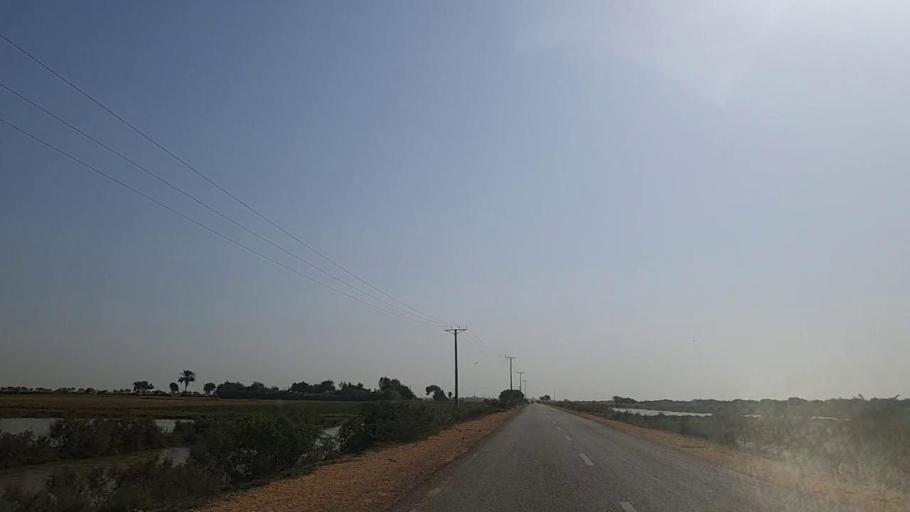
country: PK
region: Sindh
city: Mirpur Batoro
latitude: 24.5426
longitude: 68.2802
